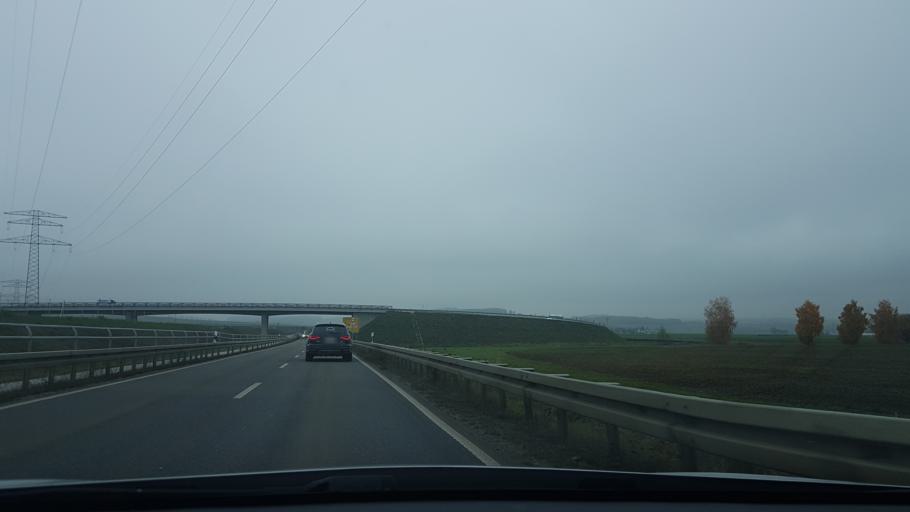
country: DE
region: Bavaria
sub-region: Lower Bavaria
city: Essenbach
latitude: 48.6095
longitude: 12.2307
